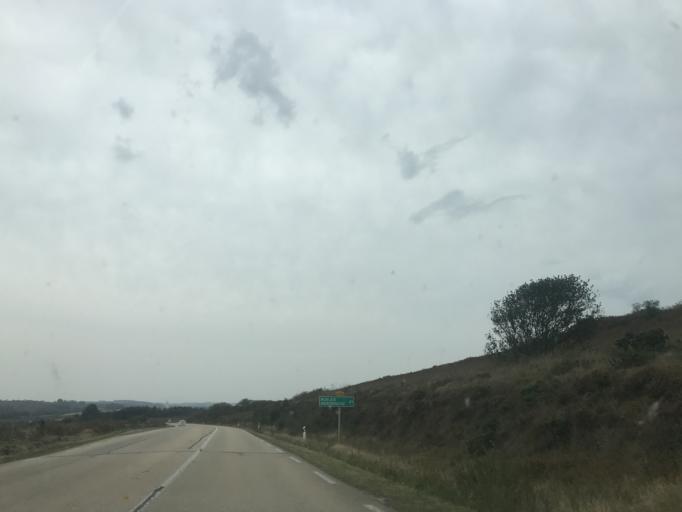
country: FR
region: Brittany
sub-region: Departement du Finistere
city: Plouneour-Menez
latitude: 48.4147
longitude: -3.8933
